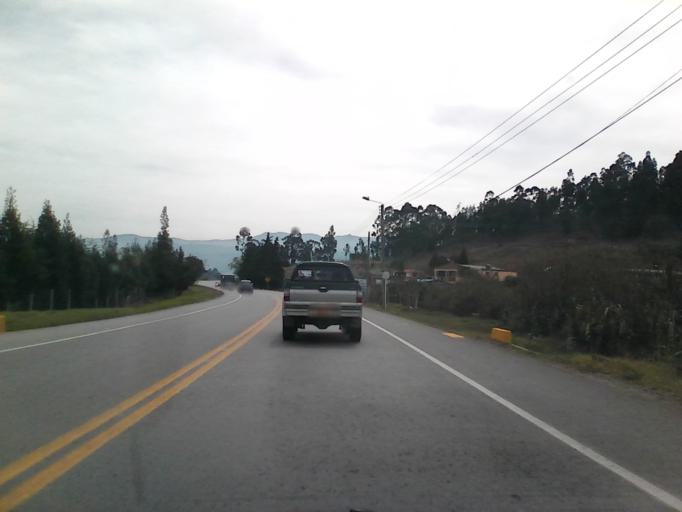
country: CO
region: Boyaca
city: Tibasosa
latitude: 5.7439
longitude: -72.9832
